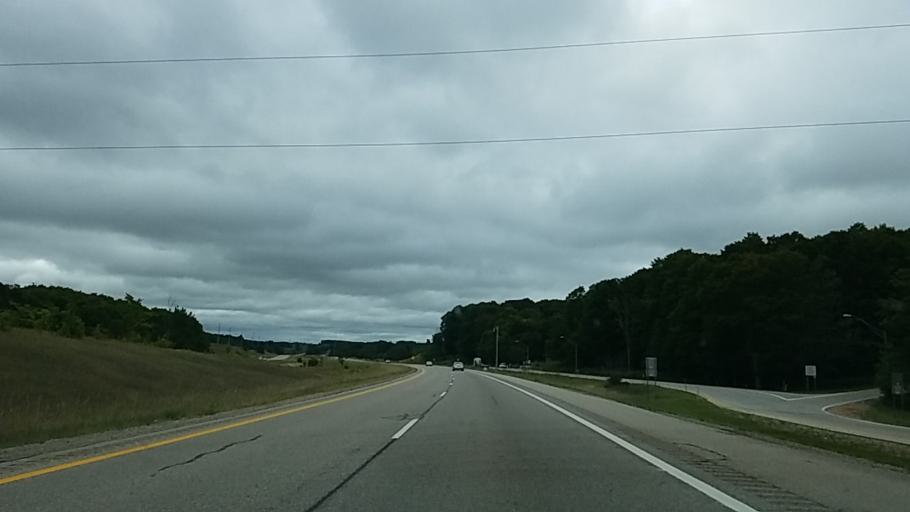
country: US
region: Michigan
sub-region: Otsego County
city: Gaylord
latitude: 45.1089
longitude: -84.6880
